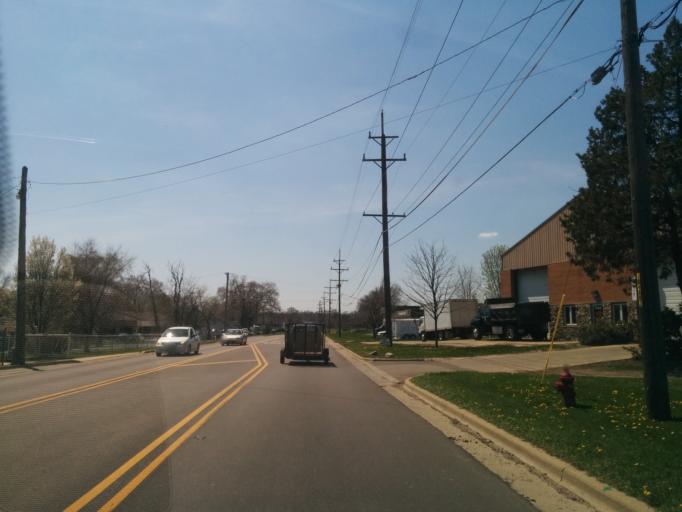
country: US
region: Illinois
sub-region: Kane County
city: South Elgin
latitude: 42.0085
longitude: -88.2916
